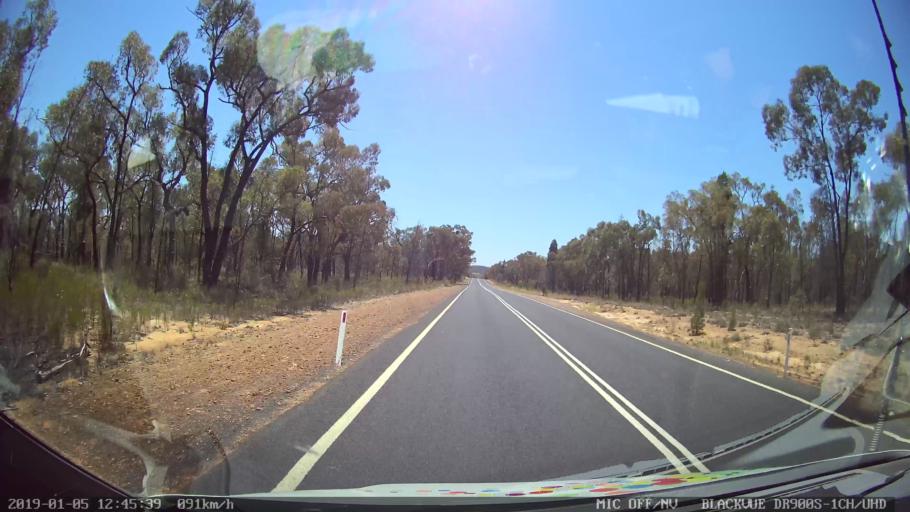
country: AU
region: New South Wales
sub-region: Warrumbungle Shire
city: Coonabarabran
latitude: -31.1257
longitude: 149.5527
